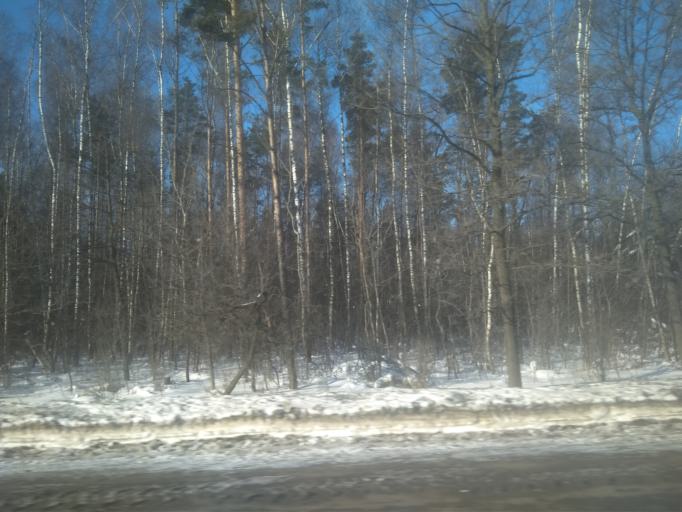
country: RU
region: Moskovskaya
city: Gorki-Leninskiye
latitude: 55.5174
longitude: 37.8256
